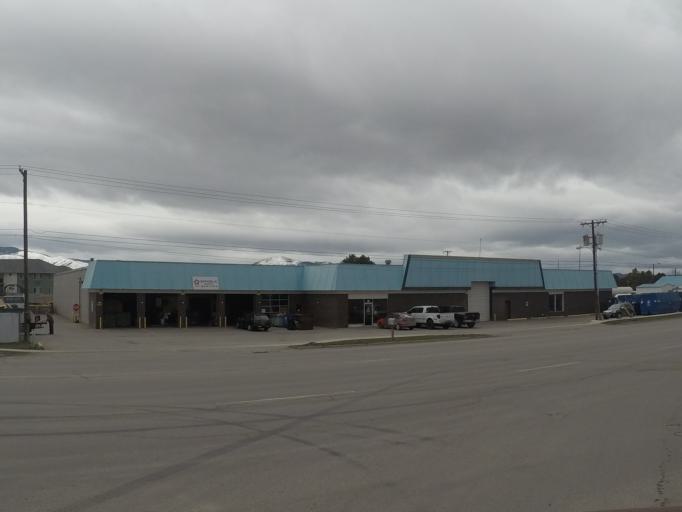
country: US
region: Montana
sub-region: Missoula County
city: Orchard Homes
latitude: 46.8959
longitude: -114.0336
